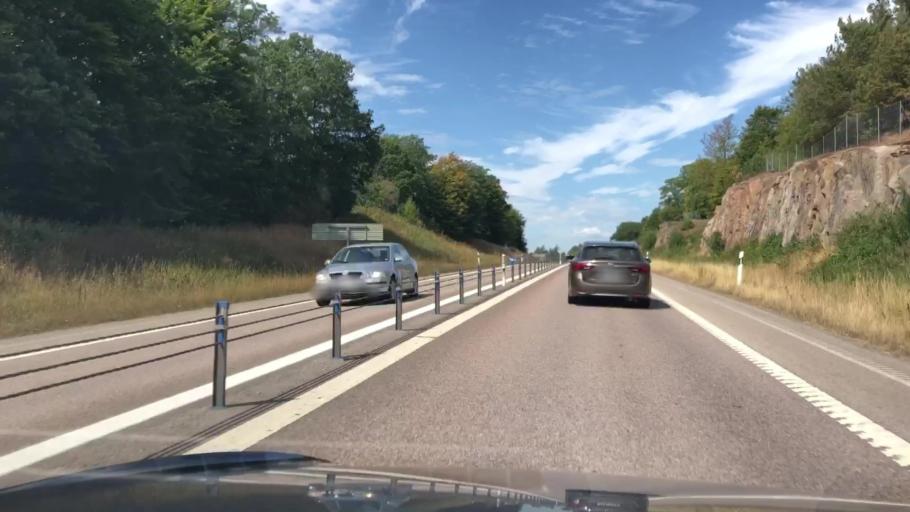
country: SE
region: Blekinge
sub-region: Ronneby Kommun
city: Kallinge
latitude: 56.2257
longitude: 15.2735
